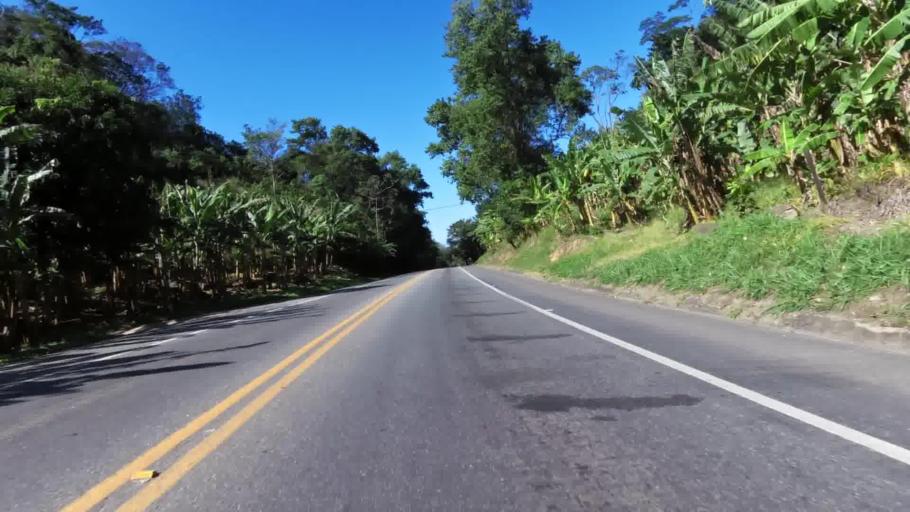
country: BR
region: Espirito Santo
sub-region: Iconha
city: Iconha
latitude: -20.7979
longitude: -40.8230
